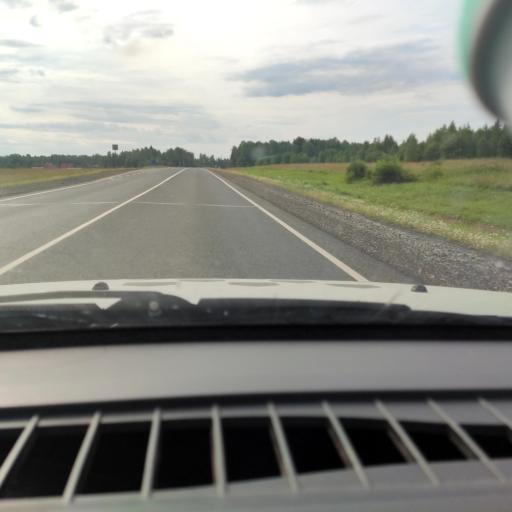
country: RU
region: Perm
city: Siva
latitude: 58.6304
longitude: 53.8642
